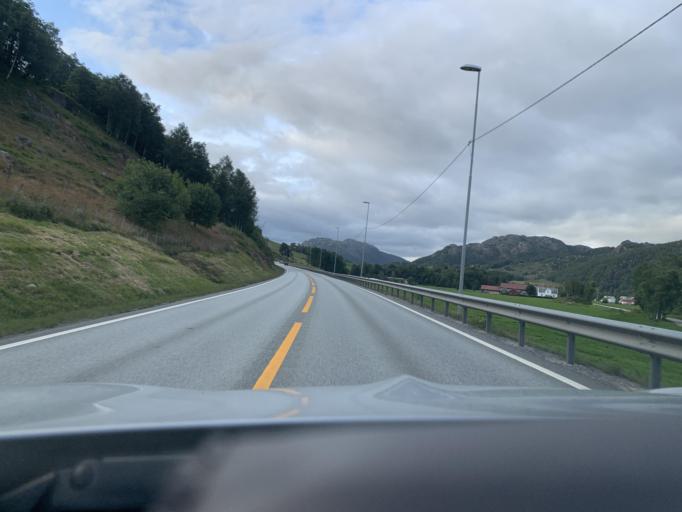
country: NO
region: Rogaland
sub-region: Bjerkreim
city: Vikesa
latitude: 58.6013
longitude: 6.0830
